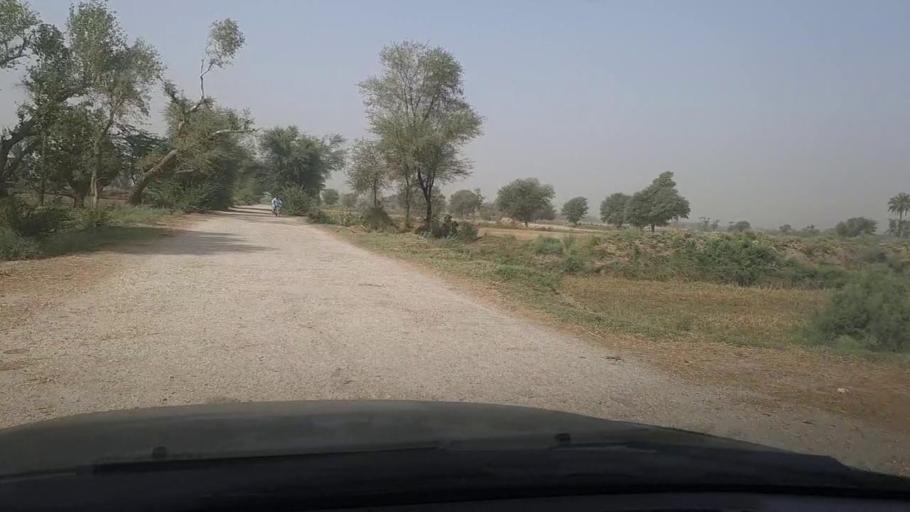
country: PK
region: Sindh
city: Shikarpur
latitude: 27.9103
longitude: 68.6023
